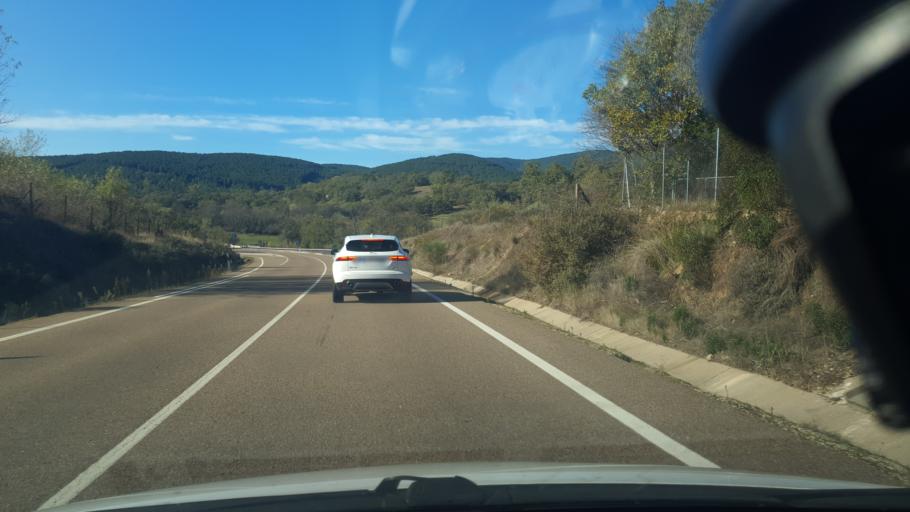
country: ES
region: Castille and Leon
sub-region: Provincia de Avila
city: Arenas de San Pedro
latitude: 40.1898
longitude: -5.0736
